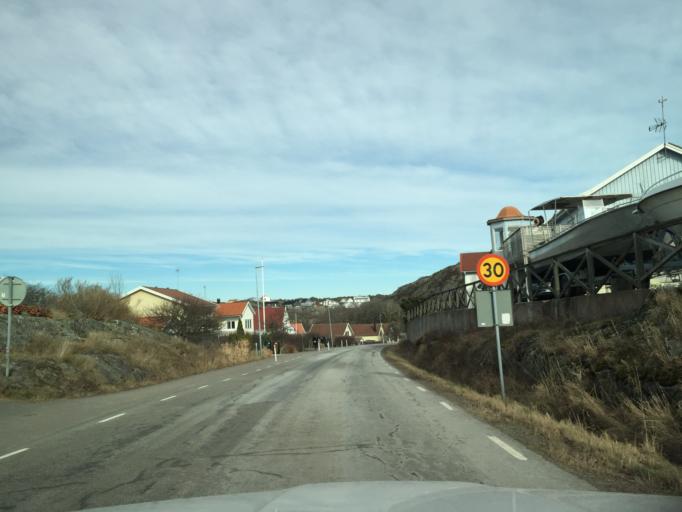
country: SE
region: Vaestra Goetaland
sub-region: Tjorns Kommun
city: Skaerhamn
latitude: 58.0170
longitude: 11.5186
